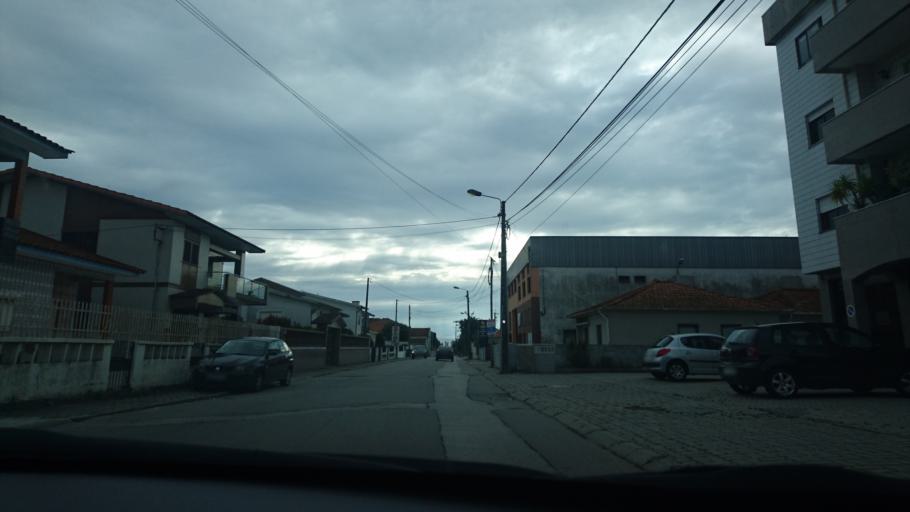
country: PT
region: Aveiro
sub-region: Ovar
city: Cortegaca
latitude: 40.9608
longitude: -8.6024
